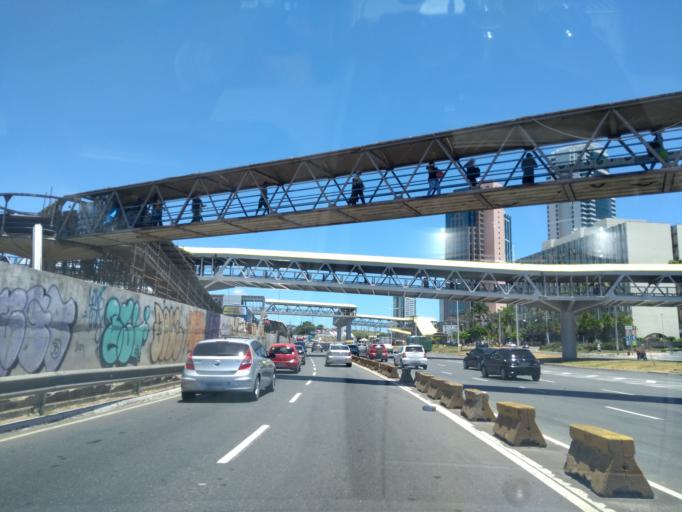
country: BR
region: Bahia
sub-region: Salvador
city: Salvador
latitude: -12.9800
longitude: -38.4649
